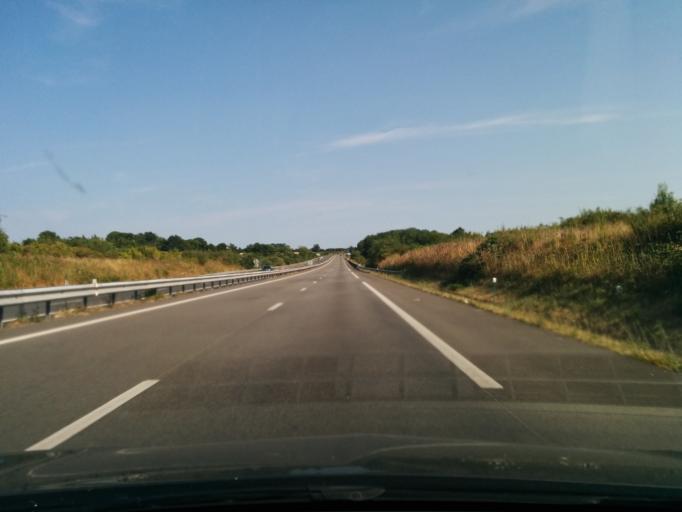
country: FR
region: Limousin
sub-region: Departement de la Haute-Vienne
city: Vicq-sur-Breuilh
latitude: 45.6643
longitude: 1.3913
